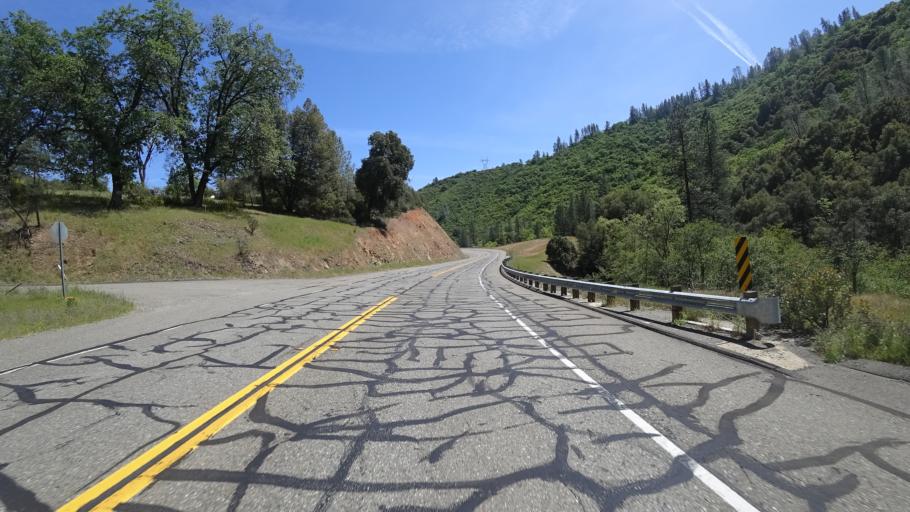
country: US
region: California
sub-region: Trinity County
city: Lewiston
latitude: 40.6725
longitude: -122.6613
